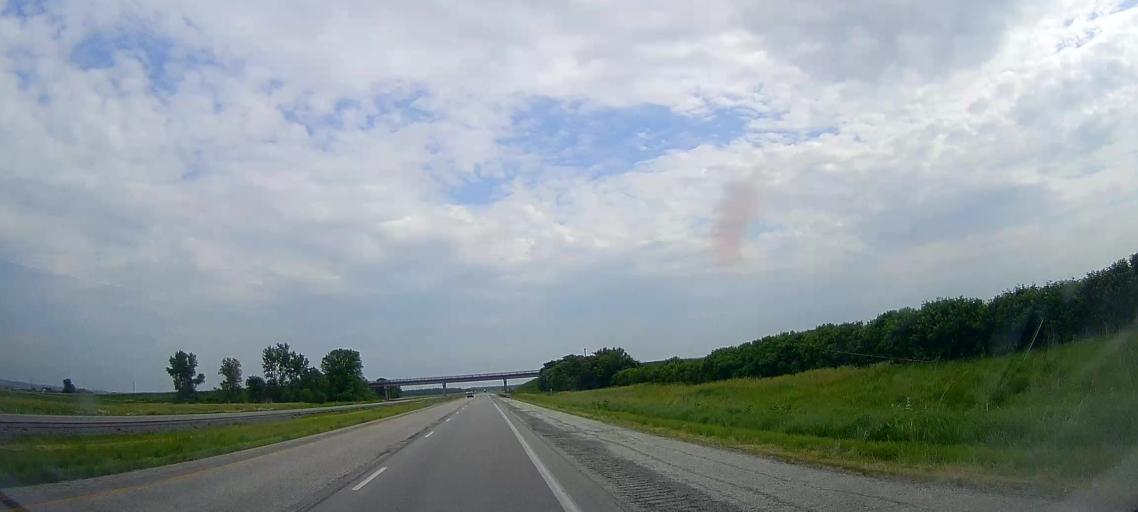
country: US
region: Nebraska
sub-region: Burt County
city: Tekamah
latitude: 41.7785
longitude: -96.0510
